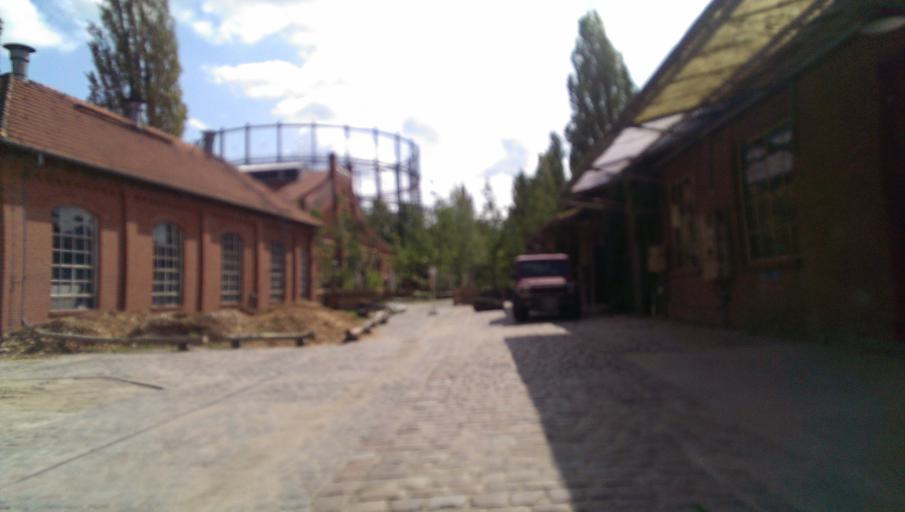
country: DE
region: Berlin
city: Mariendorf
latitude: 52.4386
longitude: 13.3670
